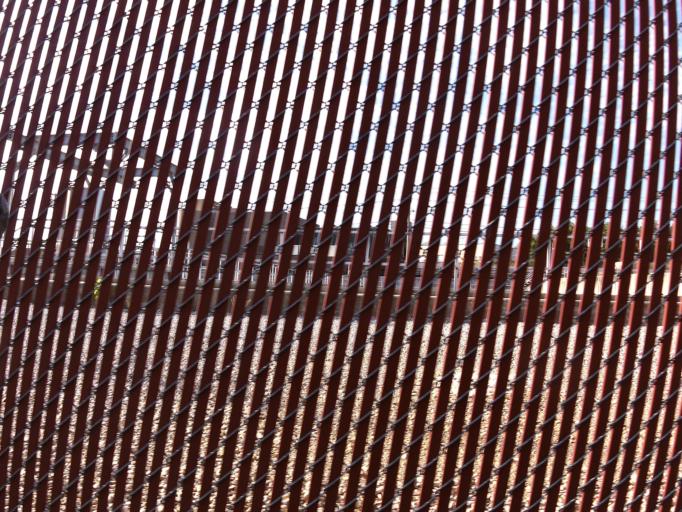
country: US
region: Tennessee
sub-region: Knox County
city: Knoxville
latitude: 35.9449
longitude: -83.9269
